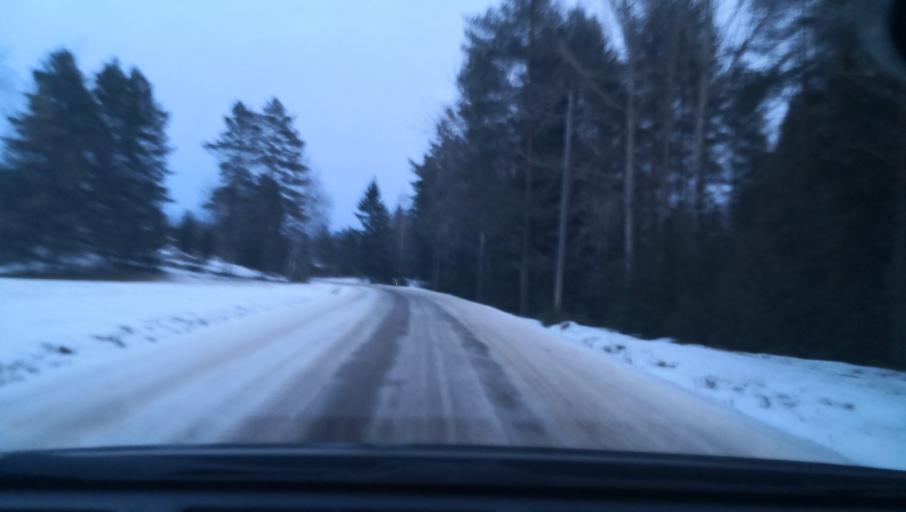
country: SE
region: Dalarna
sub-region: Avesta Kommun
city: Horndal
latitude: 60.2030
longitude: 16.5180
